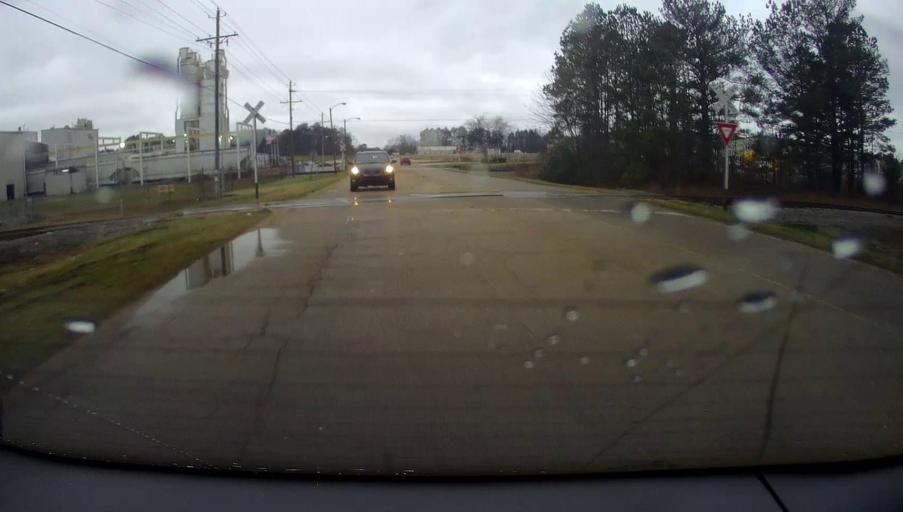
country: US
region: Mississippi
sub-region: Alcorn County
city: Corinth
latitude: 34.9088
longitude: -88.5265
